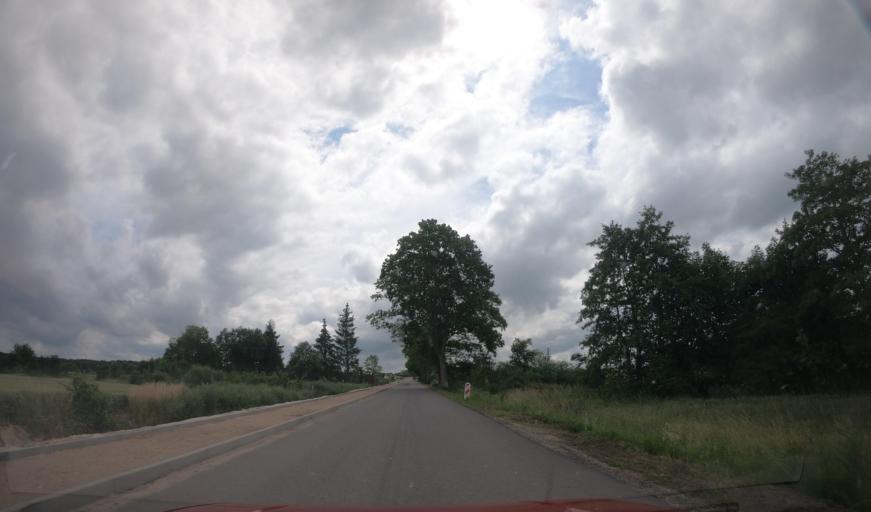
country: PL
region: West Pomeranian Voivodeship
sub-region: Powiat koszalinski
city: Mielno
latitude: 54.2310
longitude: 16.1056
